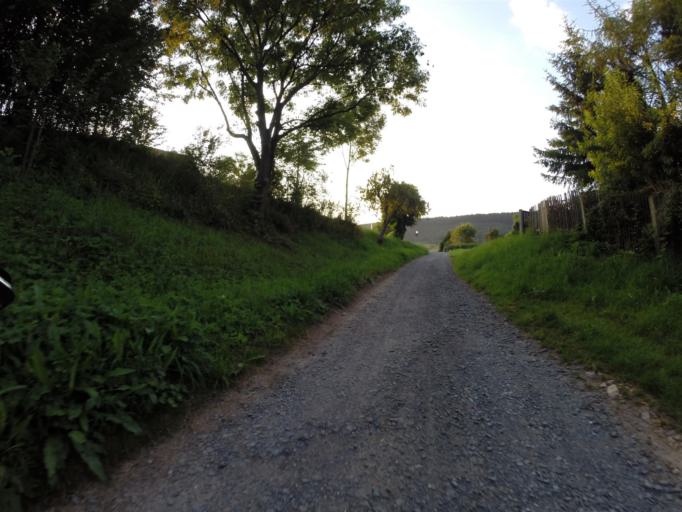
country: DE
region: Thuringia
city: Grosslobichau
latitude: 50.9295
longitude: 11.6510
